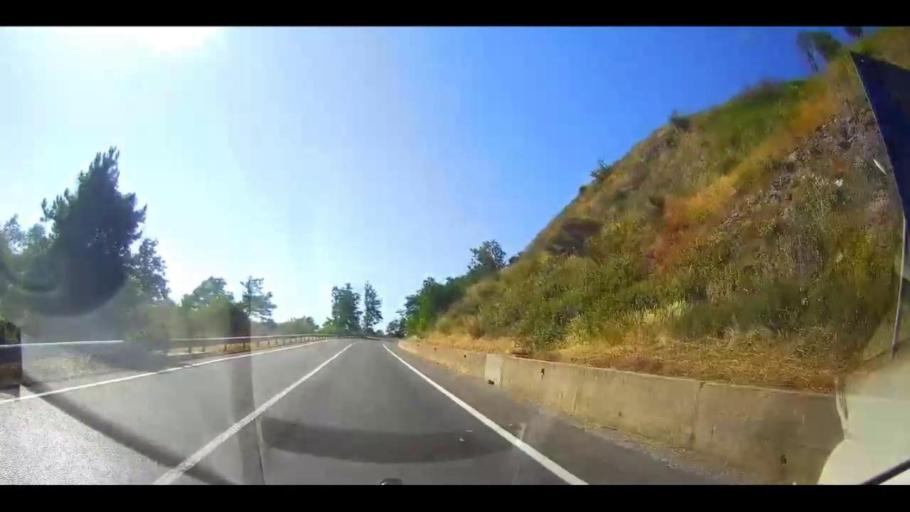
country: IT
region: Calabria
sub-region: Provincia di Cosenza
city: Celico
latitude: 39.3278
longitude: 16.3617
